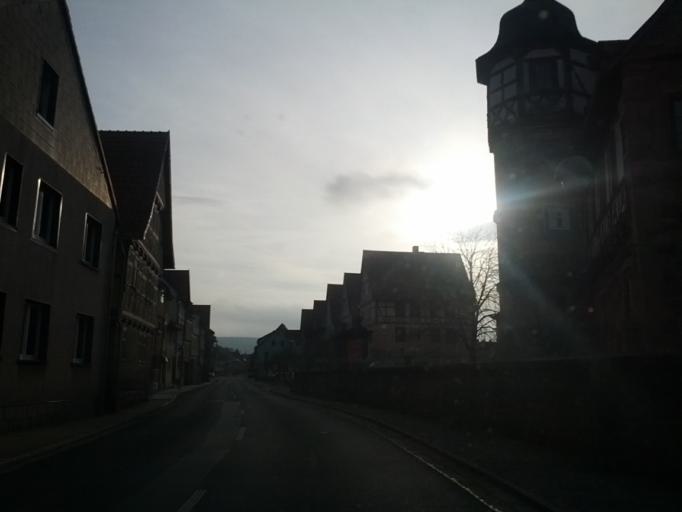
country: DE
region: Thuringia
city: Wasungen
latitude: 50.6654
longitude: 10.3665
